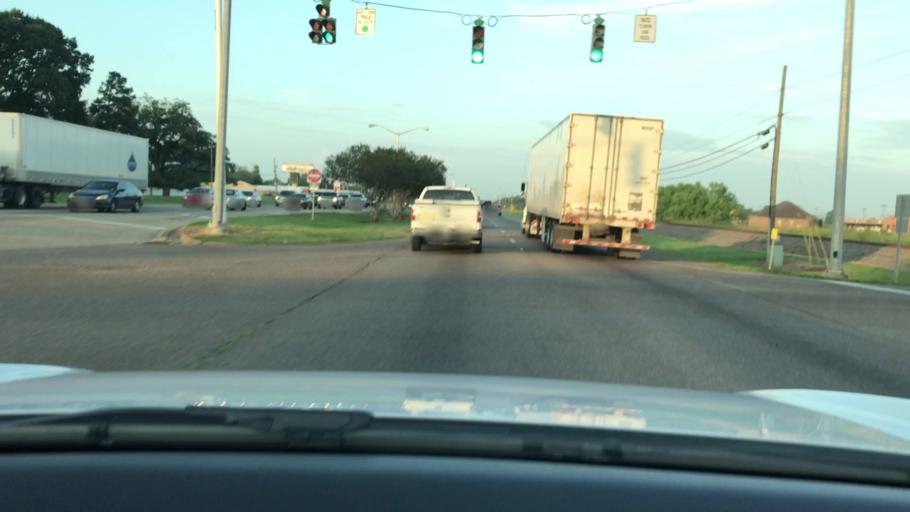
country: US
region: Louisiana
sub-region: West Baton Rouge Parish
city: Brusly
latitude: 30.3901
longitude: -91.2425
